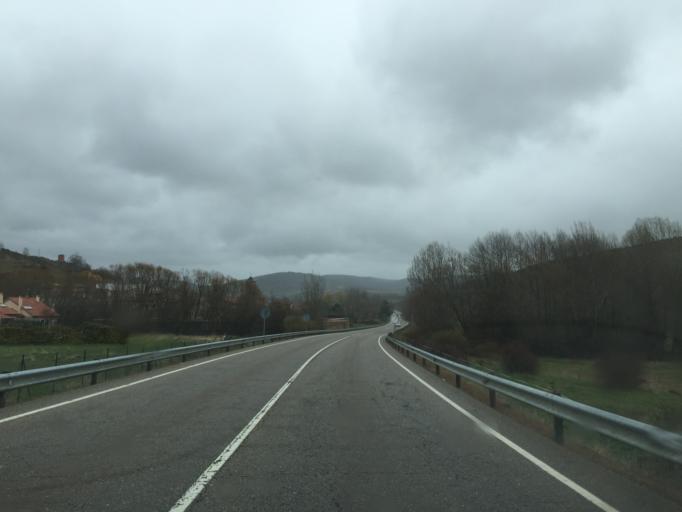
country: ES
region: Castille and Leon
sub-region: Provincia de Leon
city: Carrocera
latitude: 42.7858
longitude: -5.7736
